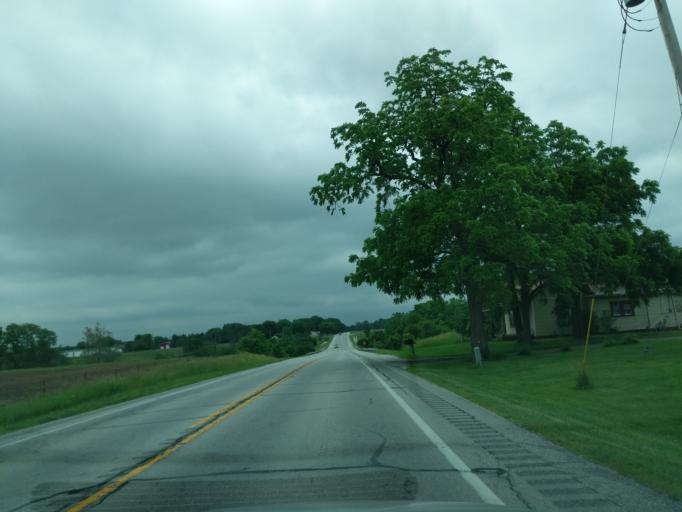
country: US
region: Indiana
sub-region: Madison County
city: Alexandria
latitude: 40.2775
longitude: -85.7155
